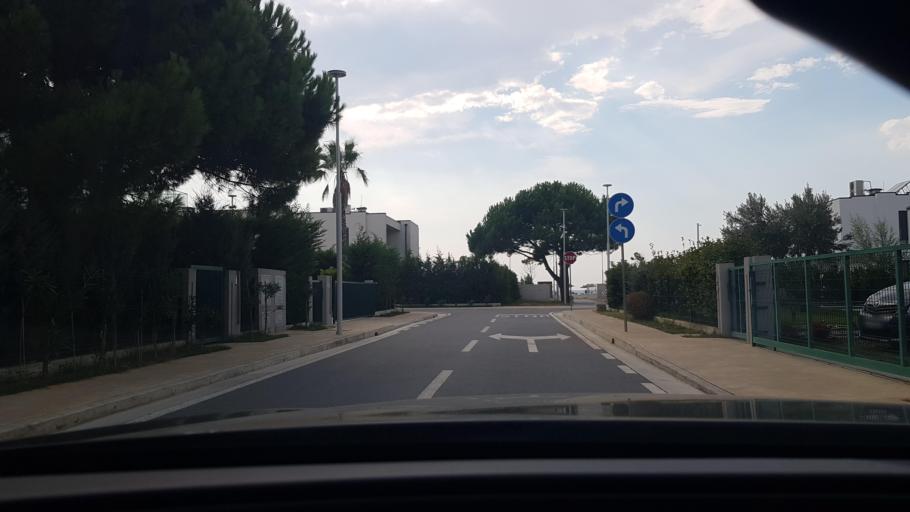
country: AL
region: Durres
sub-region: Rrethi i Durresit
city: Katundi i Ri
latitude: 41.4884
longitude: 19.5116
